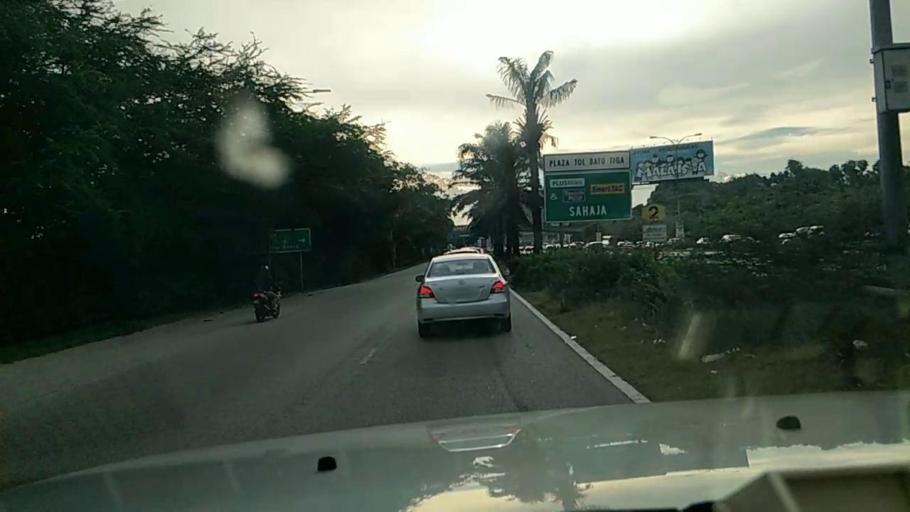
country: MY
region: Selangor
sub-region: Petaling
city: Petaling Jaya
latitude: 3.0838
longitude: 101.5970
